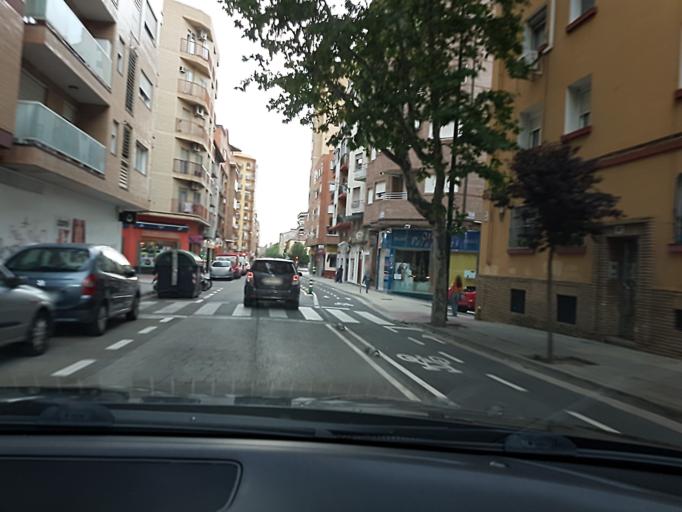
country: ES
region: Aragon
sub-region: Provincia de Zaragoza
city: Zaragoza
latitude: 41.6353
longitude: -0.8751
